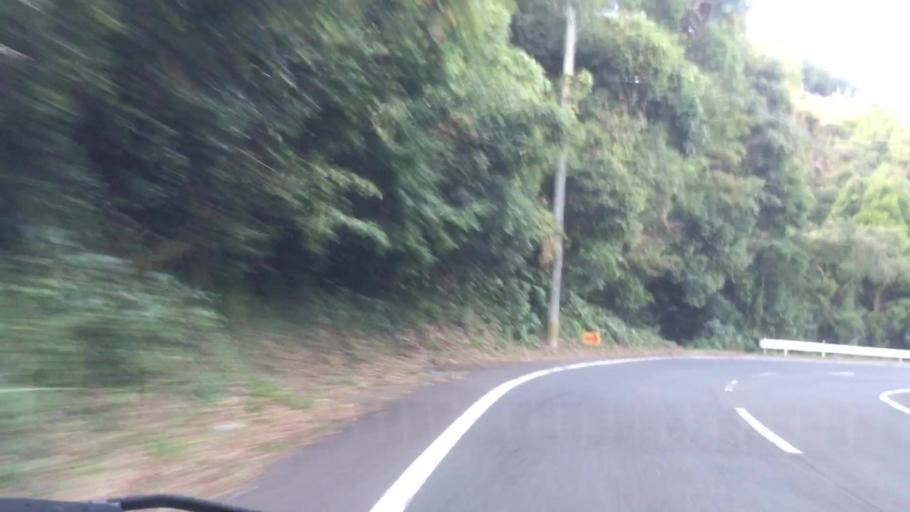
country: JP
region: Nagasaki
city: Sasebo
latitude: 32.9841
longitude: 129.7175
